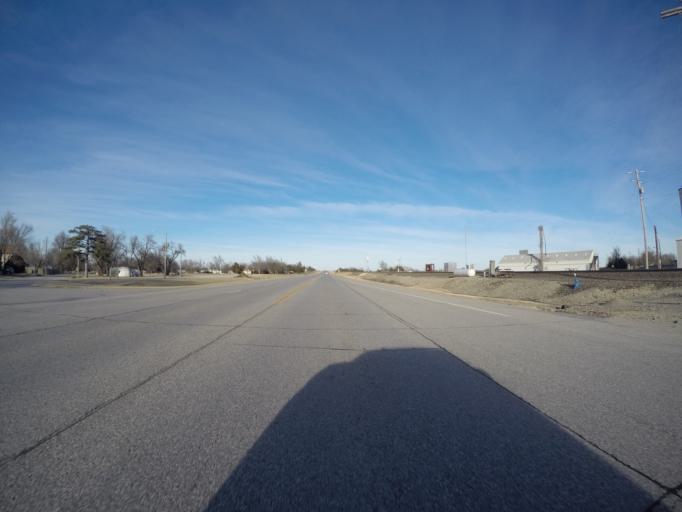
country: US
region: Kansas
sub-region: Harvey County
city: North Newton
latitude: 38.1181
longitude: -97.2555
